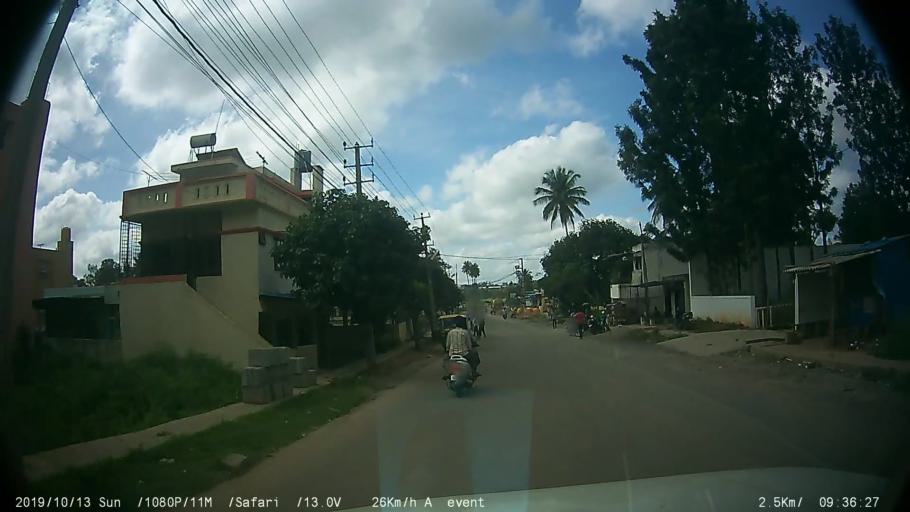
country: IN
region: Karnataka
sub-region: Bangalore Urban
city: Anekal
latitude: 12.8054
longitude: 77.6267
